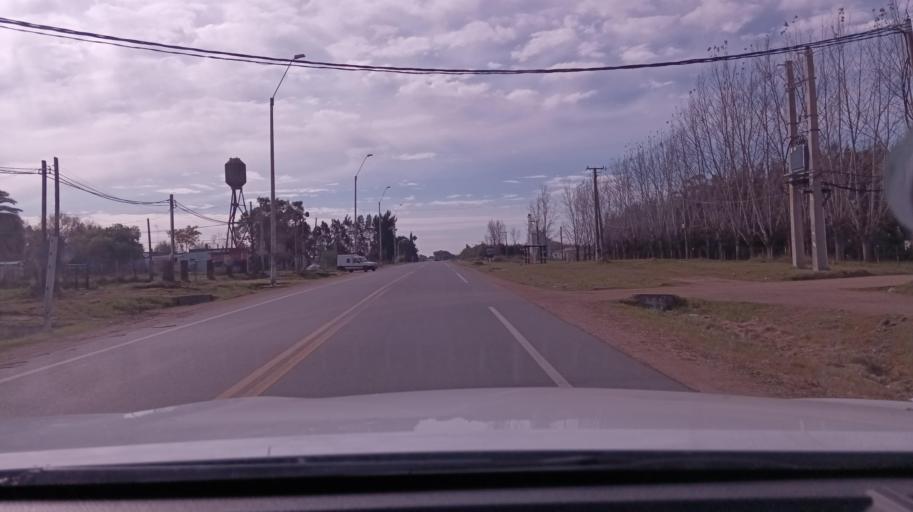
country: UY
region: Canelones
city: Toledo
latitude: -34.7343
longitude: -56.1146
